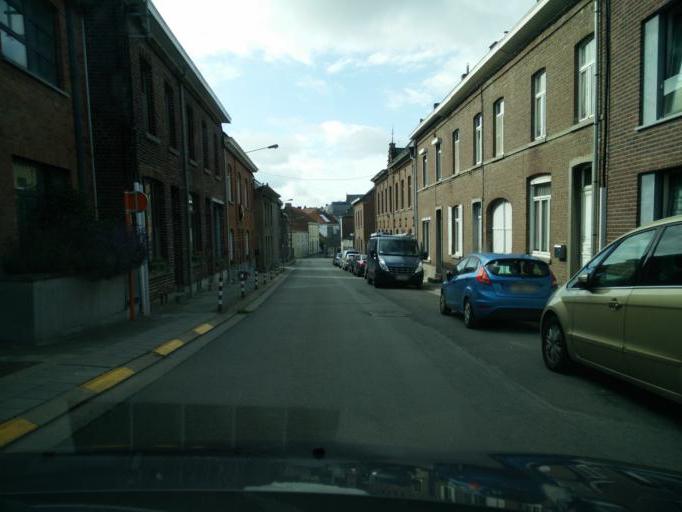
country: BE
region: Wallonia
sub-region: Province du Hainaut
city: Flobecq
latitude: 50.7395
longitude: 3.7378
